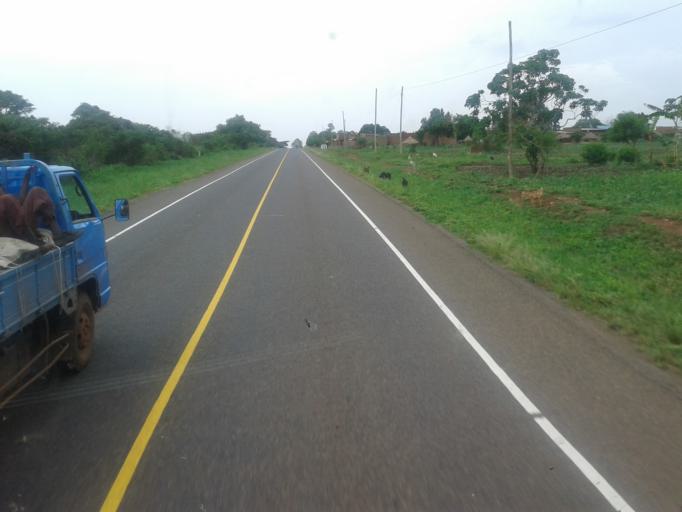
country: UG
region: Northern Region
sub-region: Oyam District
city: Oyam
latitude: 2.1442
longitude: 32.2094
